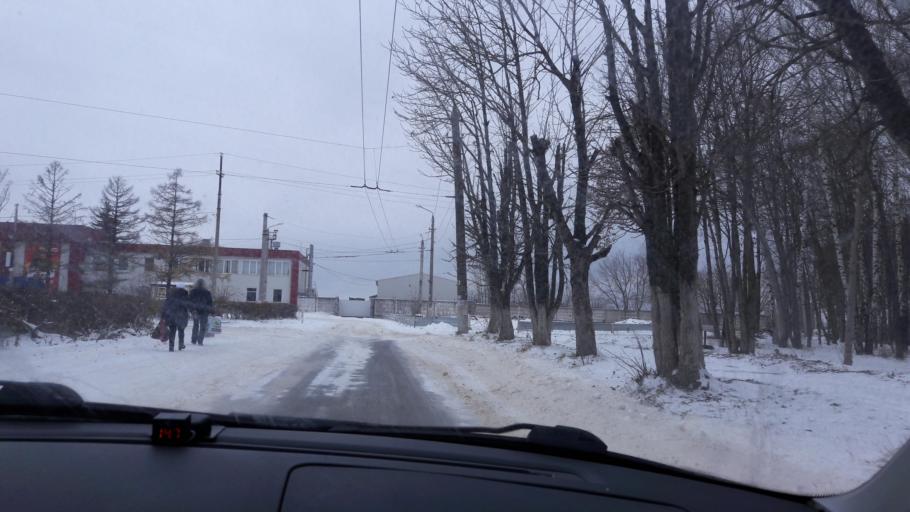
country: RU
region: Tula
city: Gorelki
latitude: 54.2342
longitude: 37.6182
